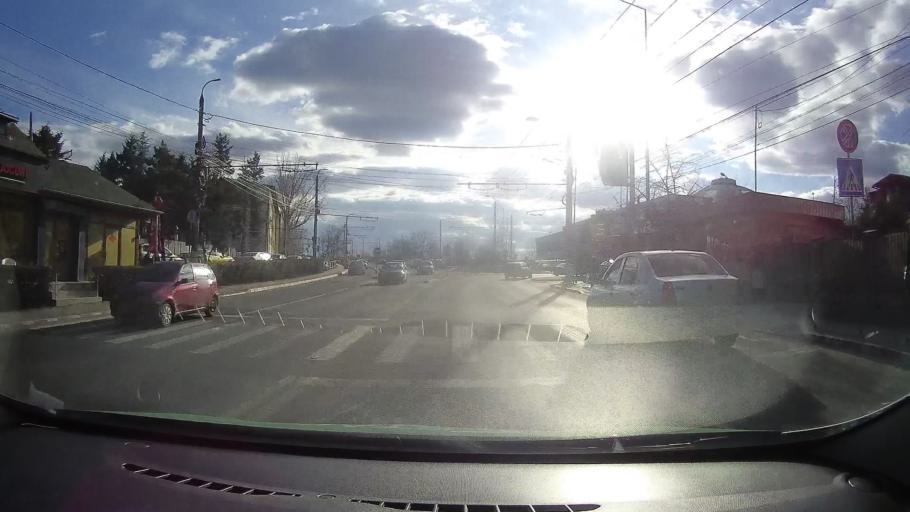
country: RO
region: Dambovita
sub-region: Comuna Lucieni
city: Lucieni
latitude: 44.8553
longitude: 25.4215
